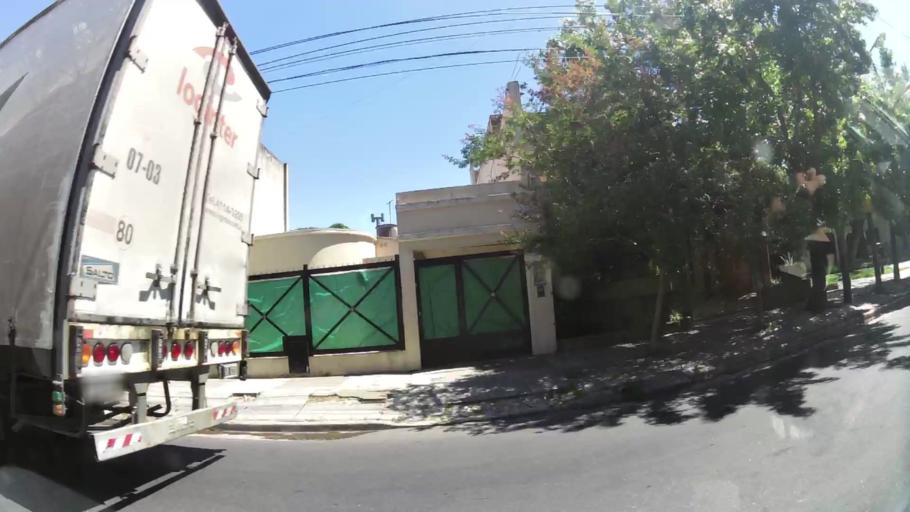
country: AR
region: Buenos Aires
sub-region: Partido de General San Martin
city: General San Martin
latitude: -34.5576
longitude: -58.5353
